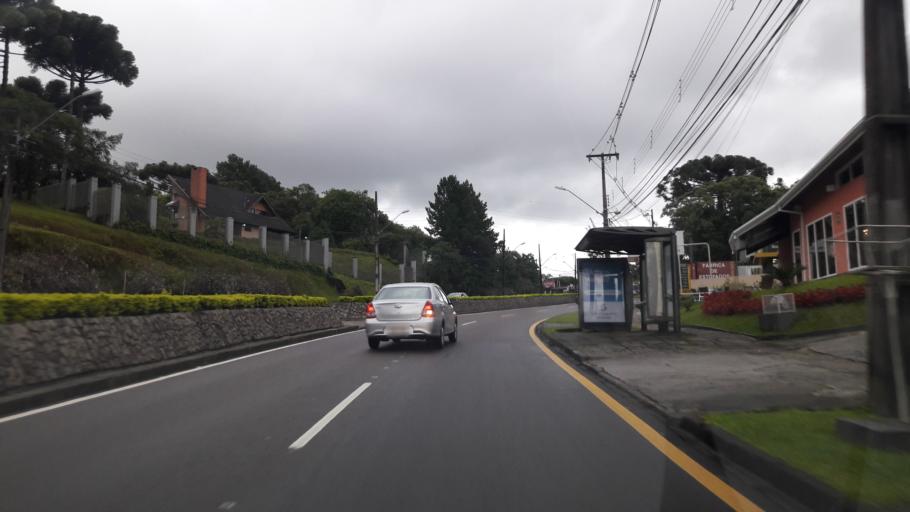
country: BR
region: Parana
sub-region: Curitiba
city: Curitiba
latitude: -25.4112
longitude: -49.3203
